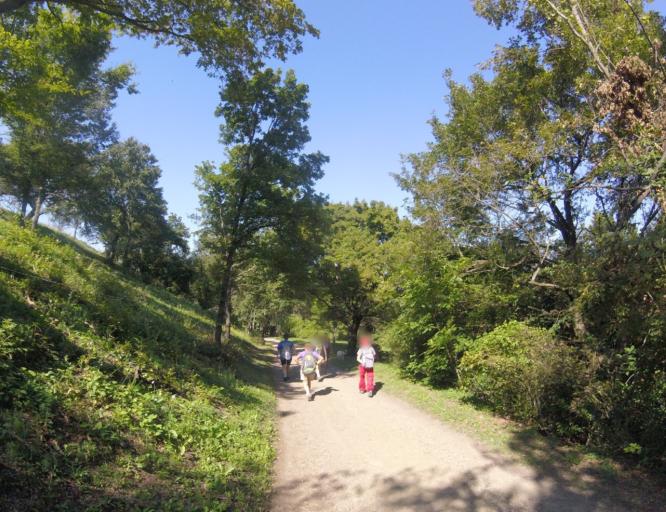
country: HU
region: Nograd
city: Rimoc
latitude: 47.9974
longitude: 19.5846
